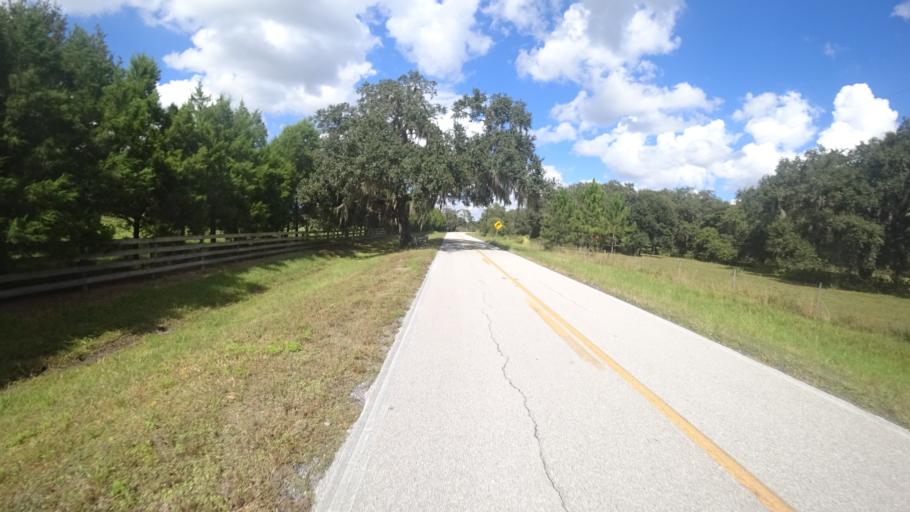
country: US
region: Florida
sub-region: Sarasota County
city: Warm Mineral Springs
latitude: 27.2573
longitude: -82.1218
